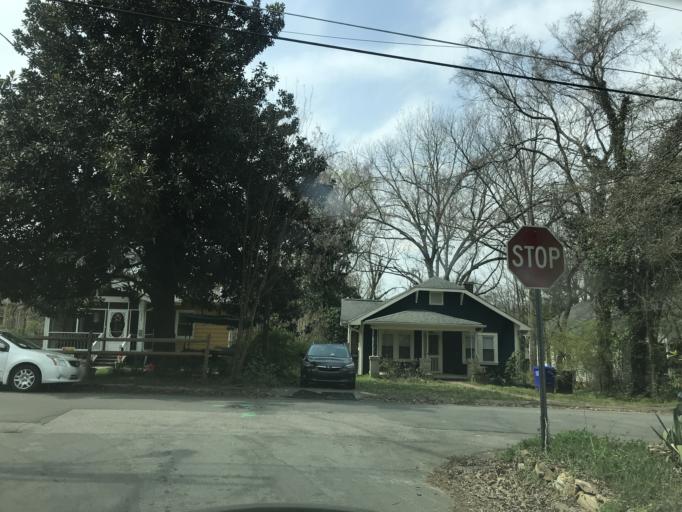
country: US
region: North Carolina
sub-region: Orange County
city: Carrboro
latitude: 35.9134
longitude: -79.0663
